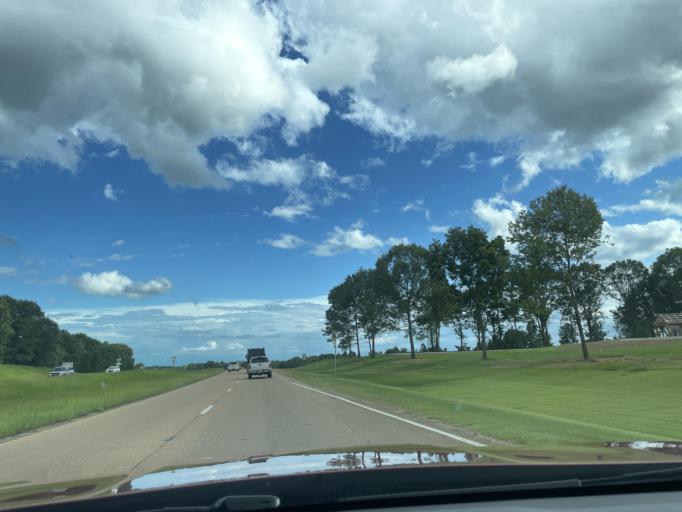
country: US
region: Mississippi
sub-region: Madison County
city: Flora
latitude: 32.5382
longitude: -90.3197
